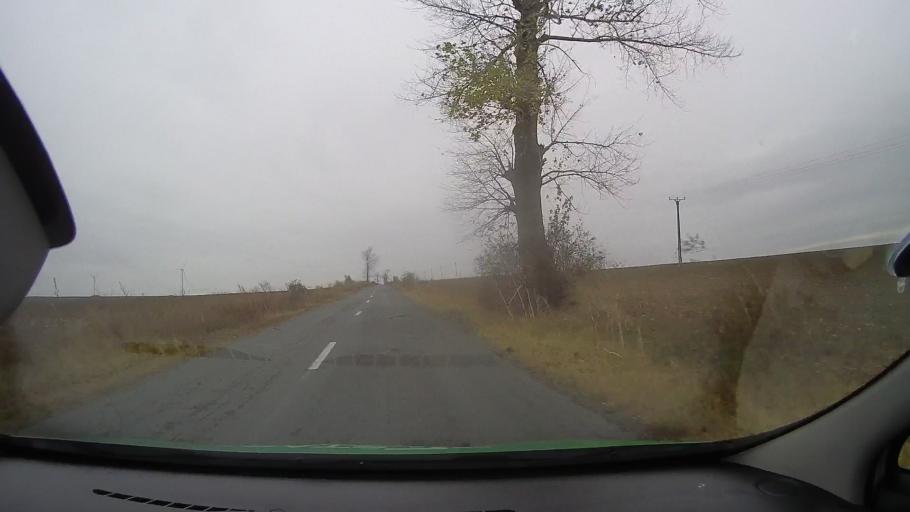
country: RO
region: Constanta
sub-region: Comuna Pantelimon
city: Pantelimon
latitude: 44.5609
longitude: 28.3216
